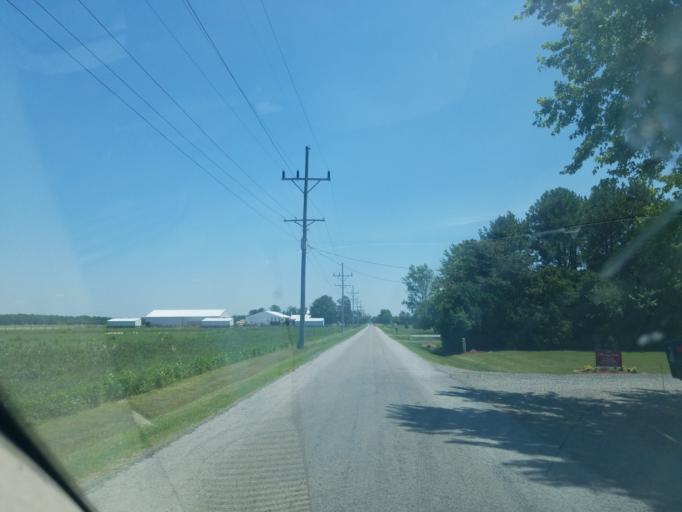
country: US
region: Ohio
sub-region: Allen County
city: Delphos
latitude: 40.7794
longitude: -84.3301
